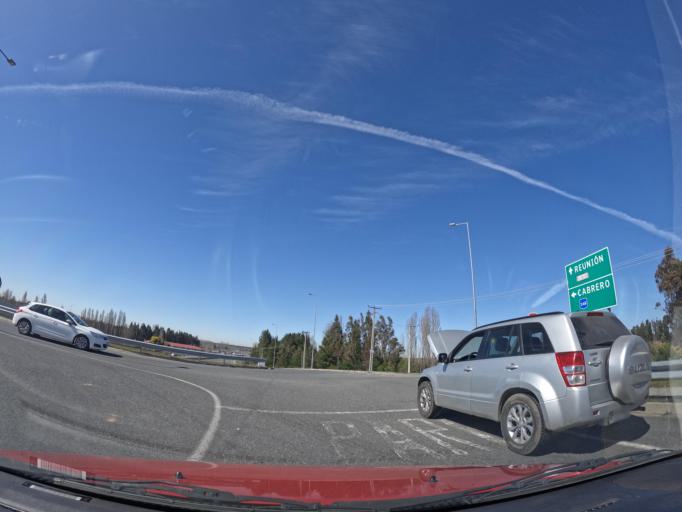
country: CL
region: Biobio
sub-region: Provincia de Biobio
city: Yumbel
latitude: -37.0027
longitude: -72.5428
